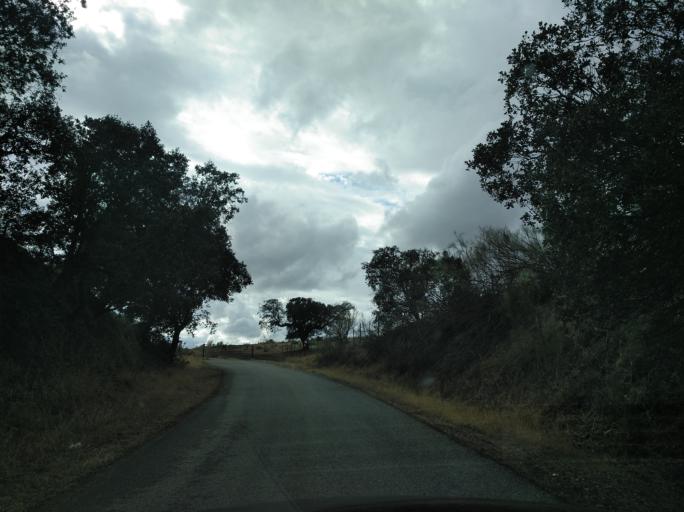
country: PT
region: Portalegre
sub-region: Campo Maior
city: Campo Maior
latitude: 39.0376
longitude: -7.1416
